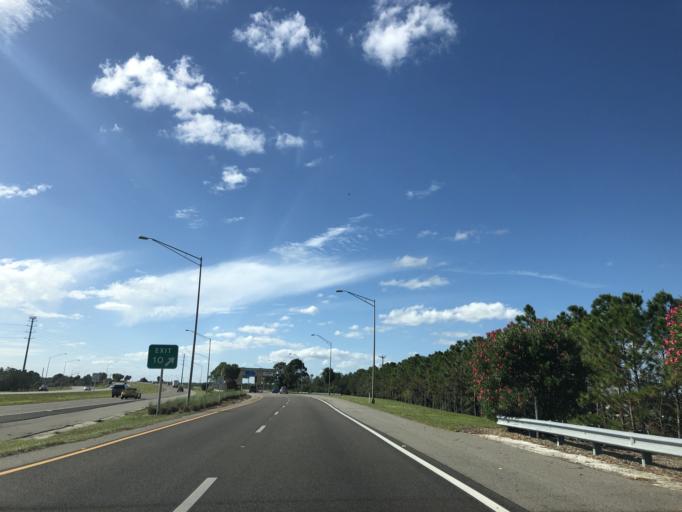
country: US
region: Florida
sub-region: Orange County
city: Hunters Creek
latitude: 28.3756
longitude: -81.4190
